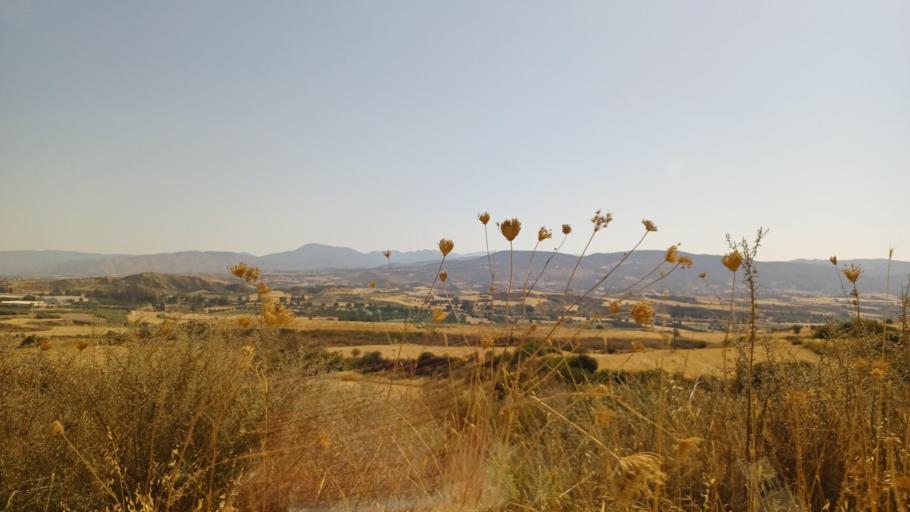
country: CY
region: Pafos
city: Polis
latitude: 35.0112
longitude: 32.4188
